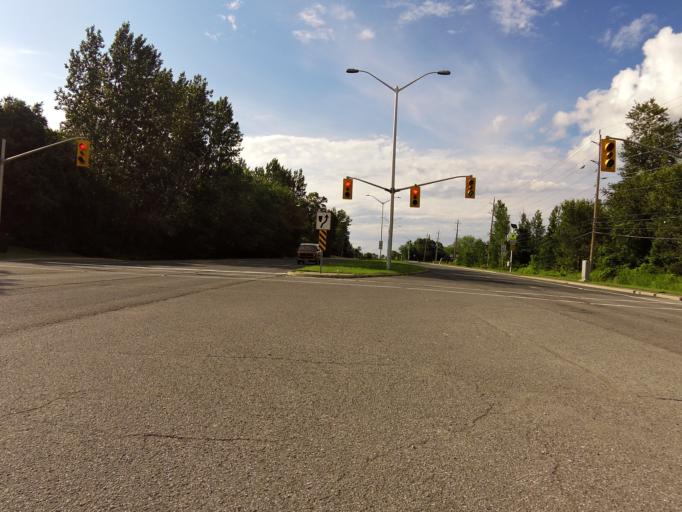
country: CA
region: Ontario
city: Bells Corners
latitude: 45.3475
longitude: -75.8446
